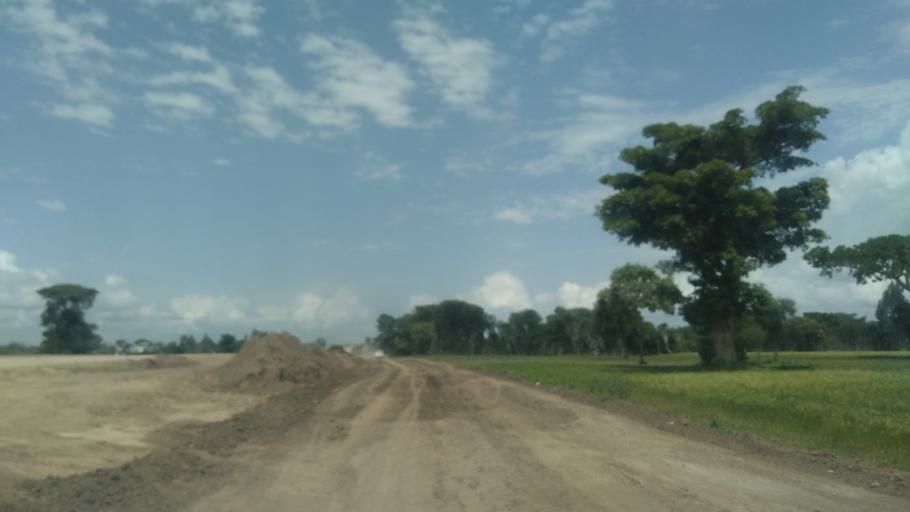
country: ET
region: Oromiya
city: Shashemene
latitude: 7.2828
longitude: 38.6066
